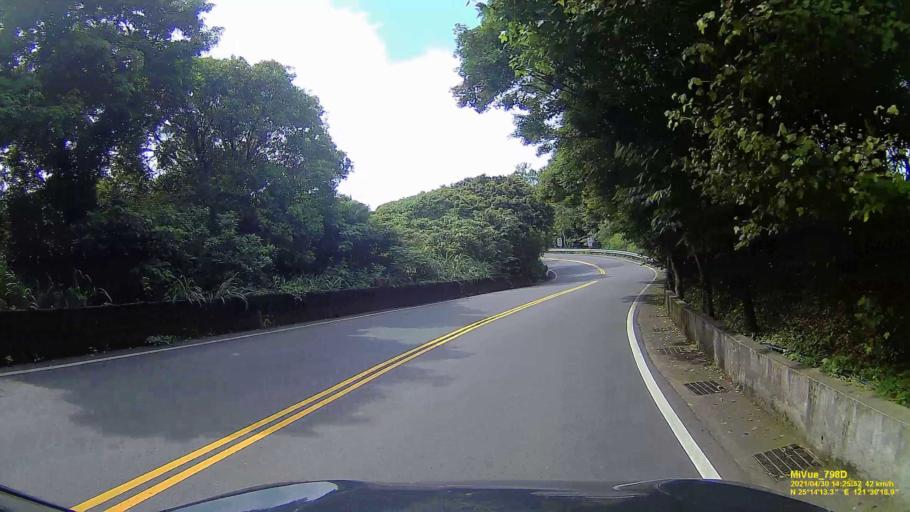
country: TW
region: Taipei
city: Taipei
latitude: 25.2373
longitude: 121.5051
